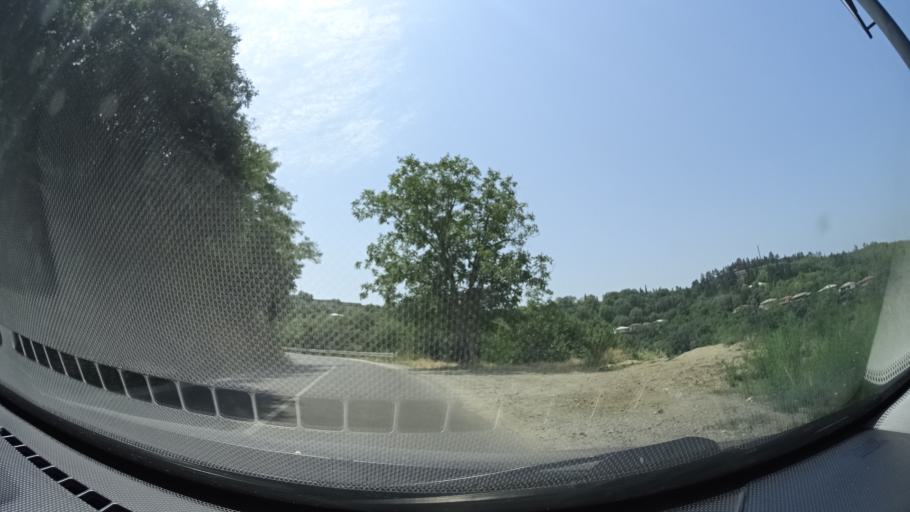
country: GE
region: Kakheti
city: Sighnaghi
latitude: 41.6244
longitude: 45.9245
